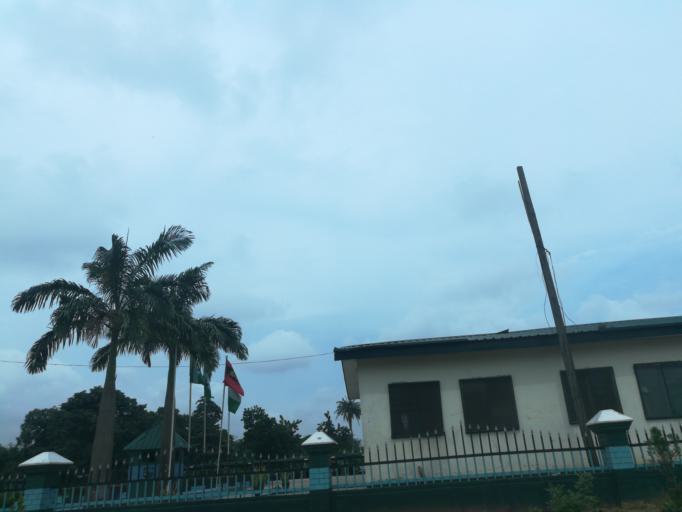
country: NG
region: Lagos
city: Oshodi
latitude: 6.5646
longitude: 3.3610
